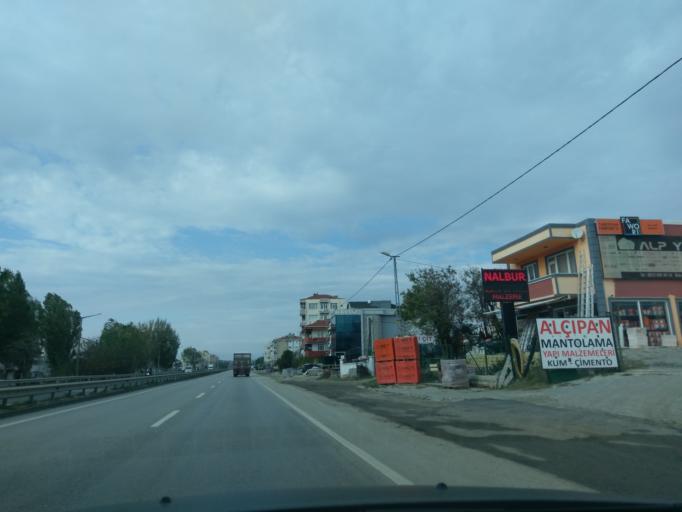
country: TR
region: Istanbul
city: Celaliye
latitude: 41.0444
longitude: 28.4124
